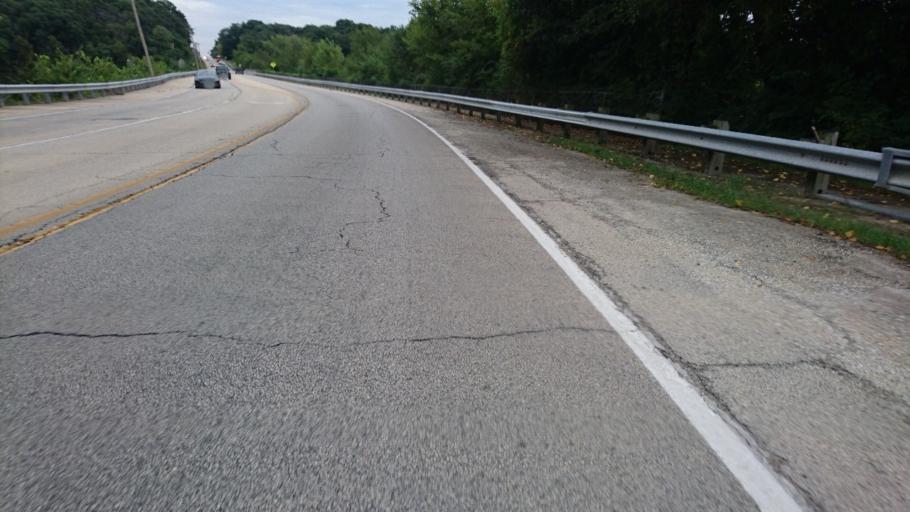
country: US
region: Illinois
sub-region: Sangamon County
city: Chatham
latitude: 39.6733
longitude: -89.6661
